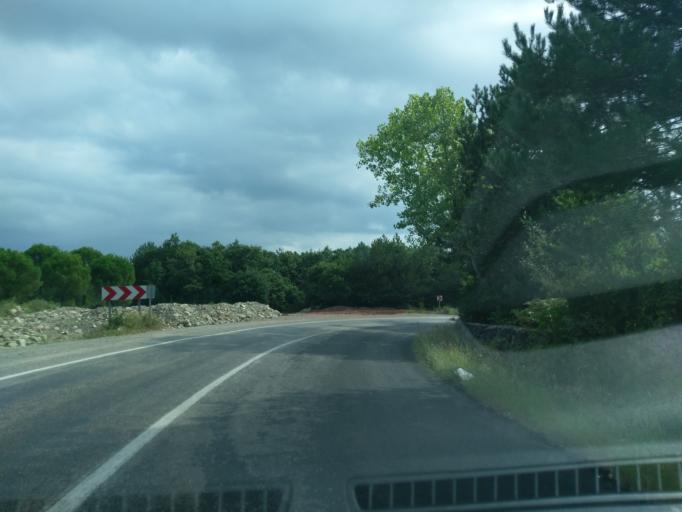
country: TR
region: Sinop
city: Yenikonak
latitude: 41.9416
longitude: 34.7125
